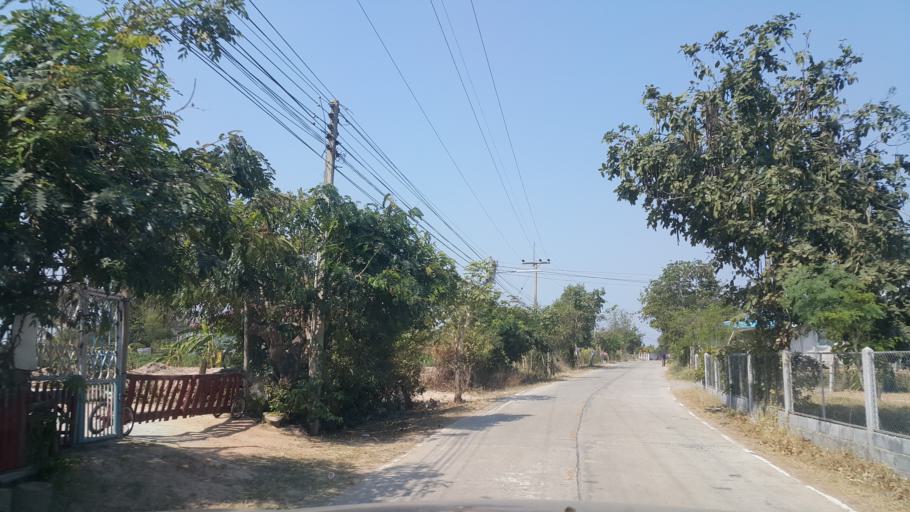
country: TH
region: Buriram
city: Satuek
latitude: 15.1373
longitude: 103.3441
